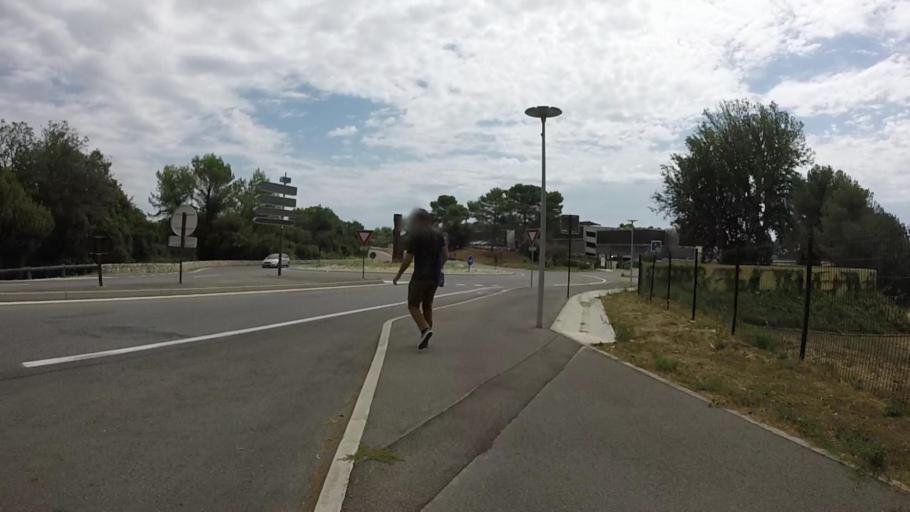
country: FR
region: Provence-Alpes-Cote d'Azur
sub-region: Departement des Alpes-Maritimes
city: Biot
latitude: 43.6141
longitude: 7.0881
